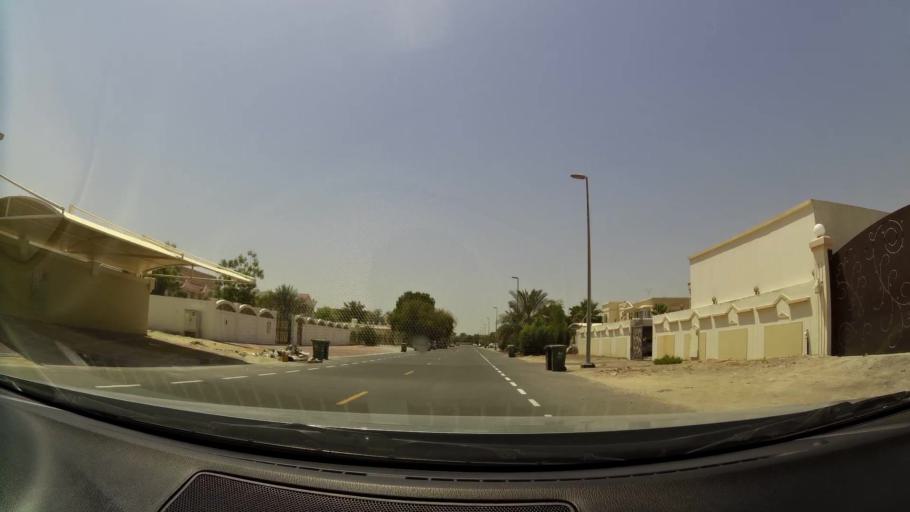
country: AE
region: Dubai
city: Dubai
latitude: 25.0962
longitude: 55.2182
